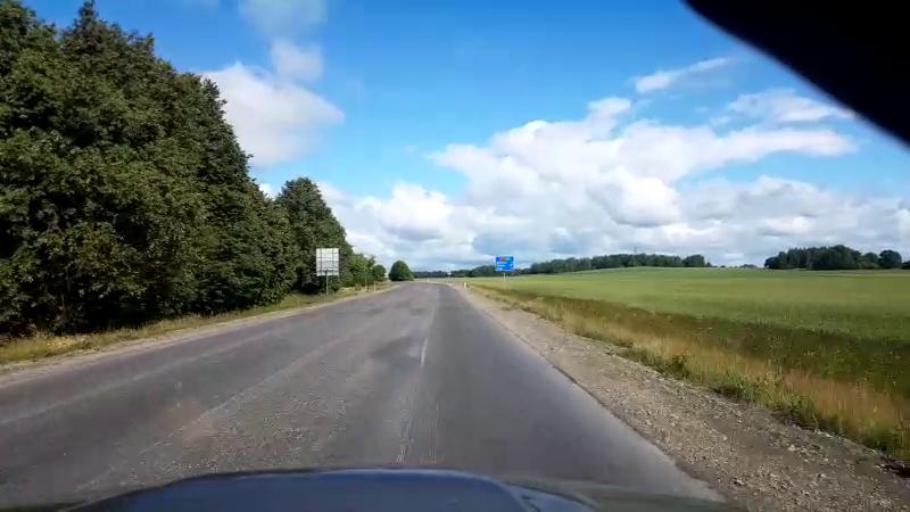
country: LV
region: Bauskas Rajons
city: Bauska
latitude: 56.3887
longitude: 24.2514
